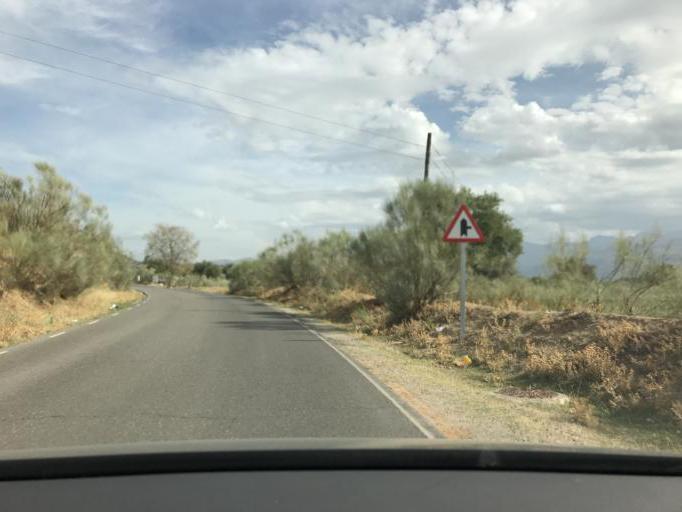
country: ES
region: Andalusia
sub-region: Provincia de Granada
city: Jun
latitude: 37.1967
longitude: -3.5729
